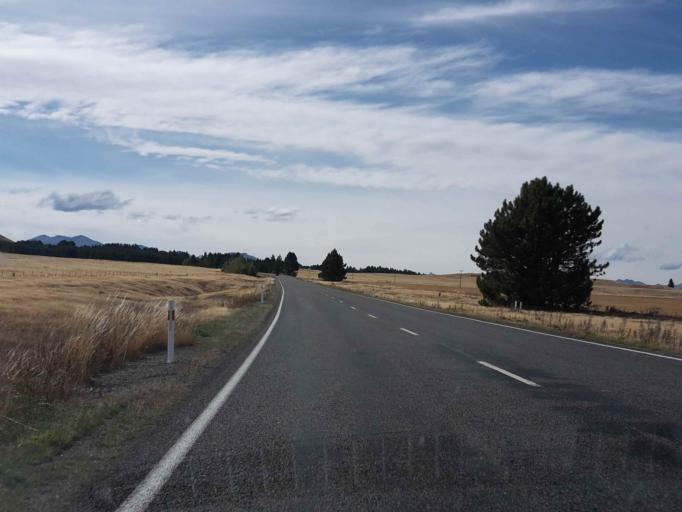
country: NZ
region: Canterbury
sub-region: Timaru District
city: Pleasant Point
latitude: -44.0240
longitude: 170.4011
